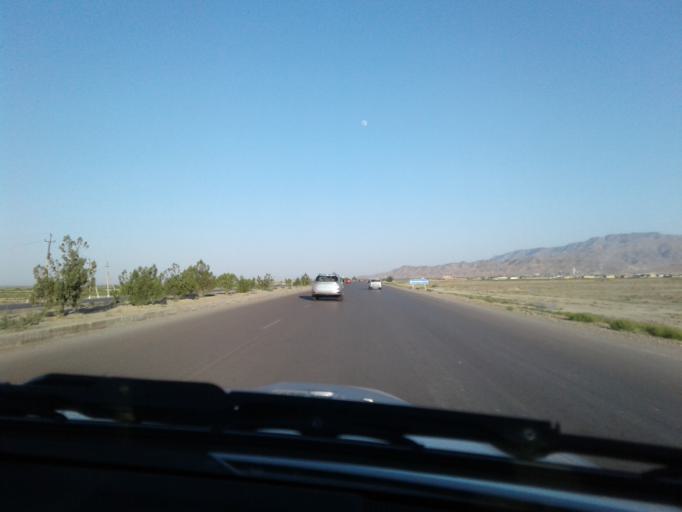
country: TM
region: Ahal
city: Baharly
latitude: 38.3118
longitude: 57.6114
